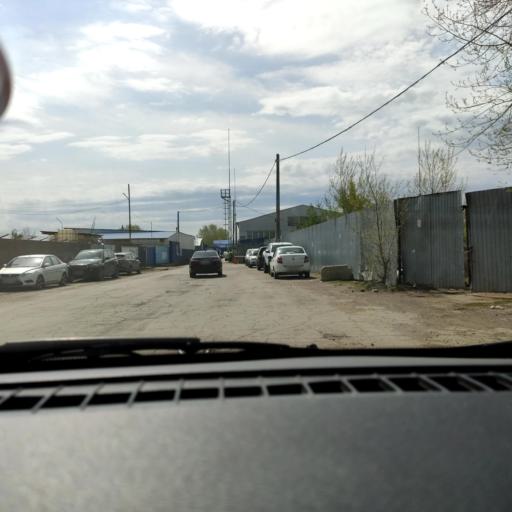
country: RU
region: Samara
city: Samara
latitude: 53.1762
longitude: 50.1235
